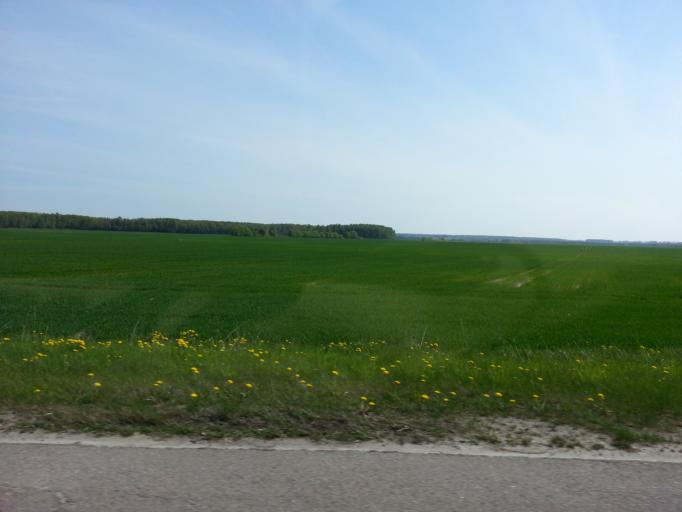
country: LT
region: Vilnius County
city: Ukmerge
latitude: 55.3294
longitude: 24.7665
